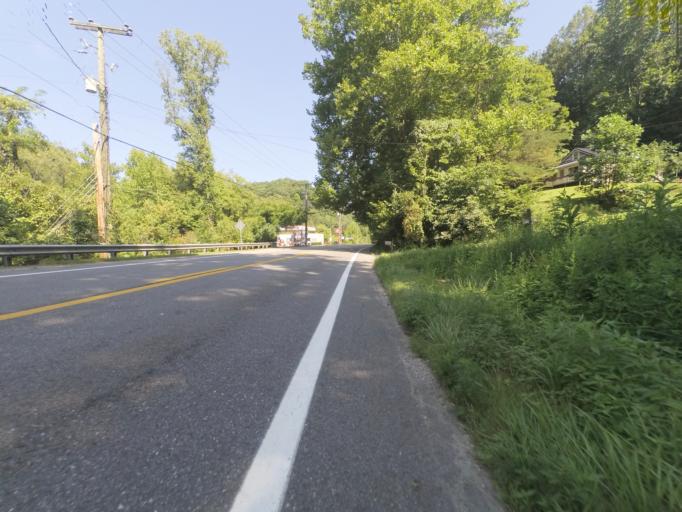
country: US
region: West Virginia
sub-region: Cabell County
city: Huntington
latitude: 38.3814
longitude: -82.4567
